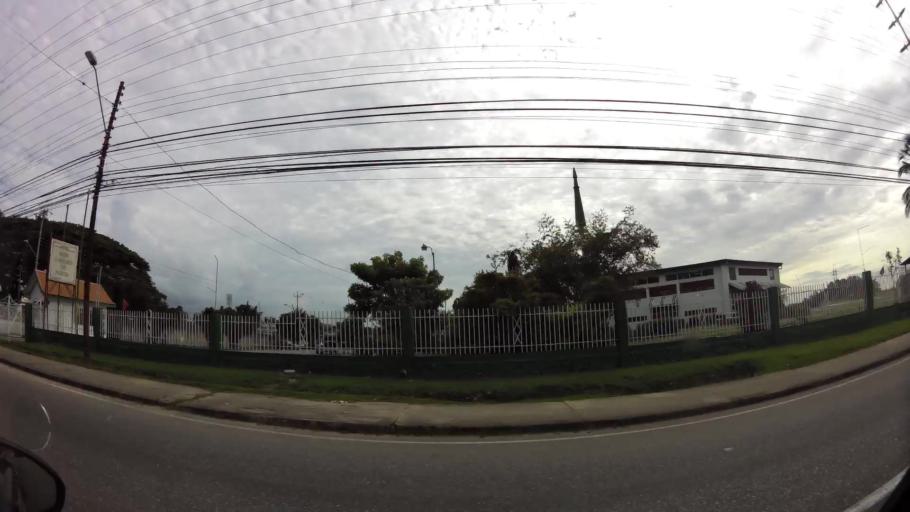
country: TT
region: City of Port of Spain
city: Mucurapo
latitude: 10.6678
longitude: -61.5341
